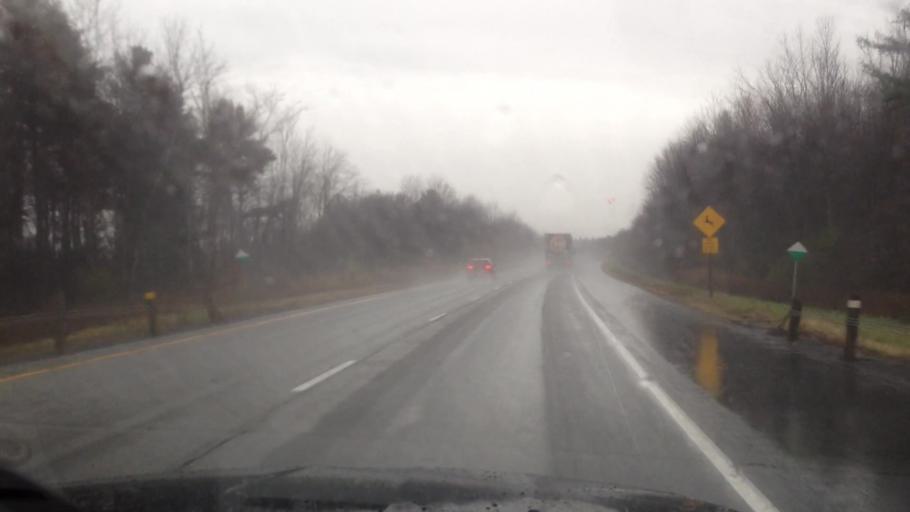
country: CA
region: Ontario
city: Bourget
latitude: 45.3136
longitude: -75.2290
